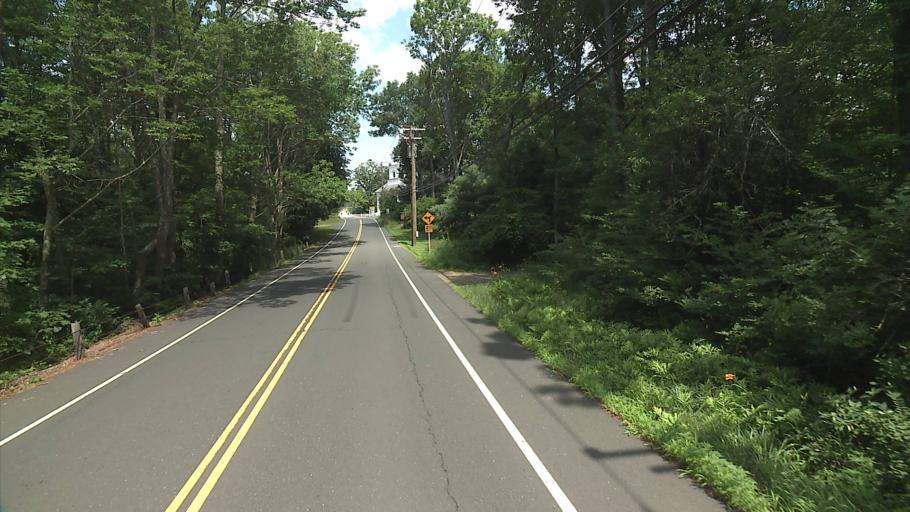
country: US
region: Connecticut
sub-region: Litchfield County
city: Winsted
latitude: 41.9876
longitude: -73.0963
